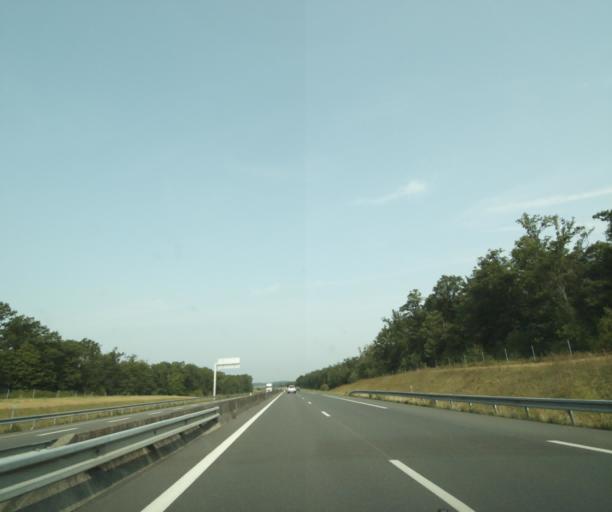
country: FR
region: Pays de la Loire
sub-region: Departement de la Sarthe
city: Champfleur
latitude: 48.3155
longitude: 0.1349
